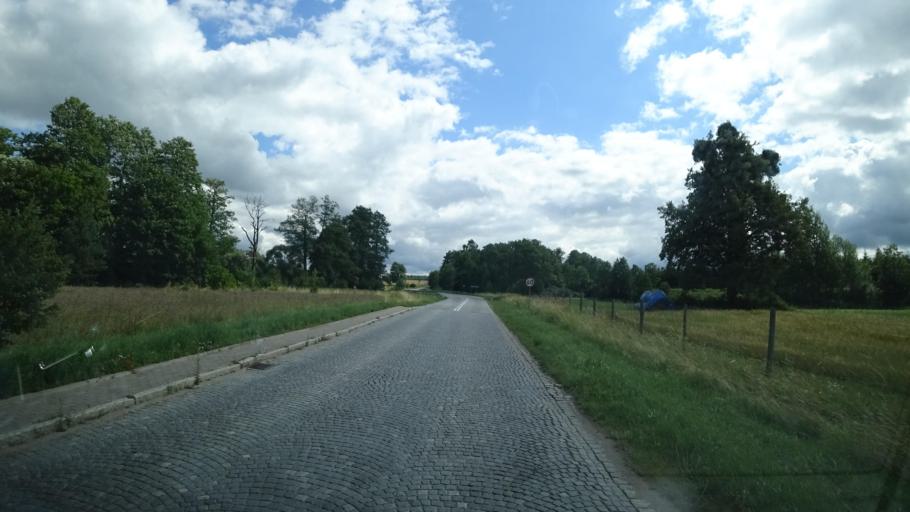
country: PL
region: Warmian-Masurian Voivodeship
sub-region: Powiat goldapski
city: Banie Mazurskie
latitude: 54.2157
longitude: 22.1565
